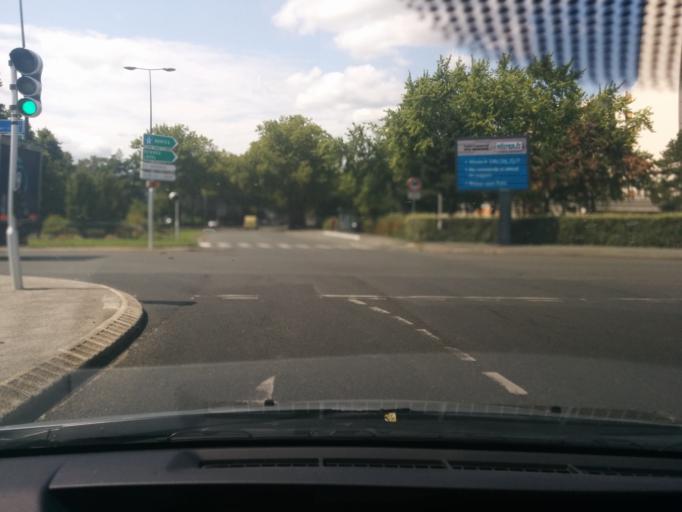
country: FR
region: Pays de la Loire
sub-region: Departement de Maine-et-Loire
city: Angers
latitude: 47.4527
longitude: -0.5408
